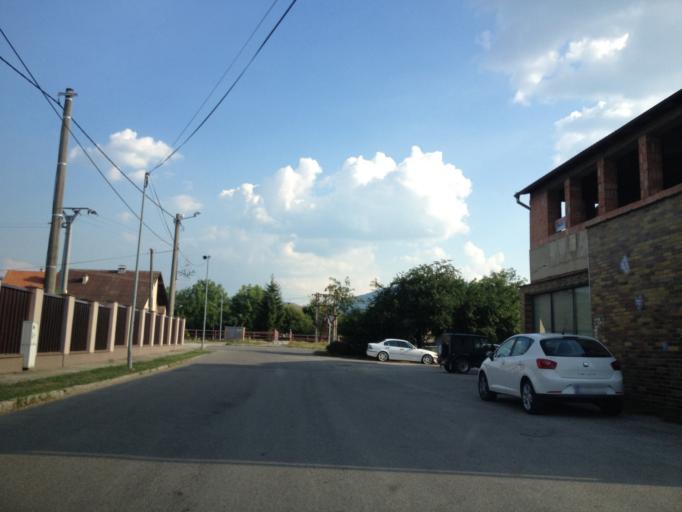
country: SK
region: Nitriansky
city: Puchov
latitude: 49.0687
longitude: 18.3321
